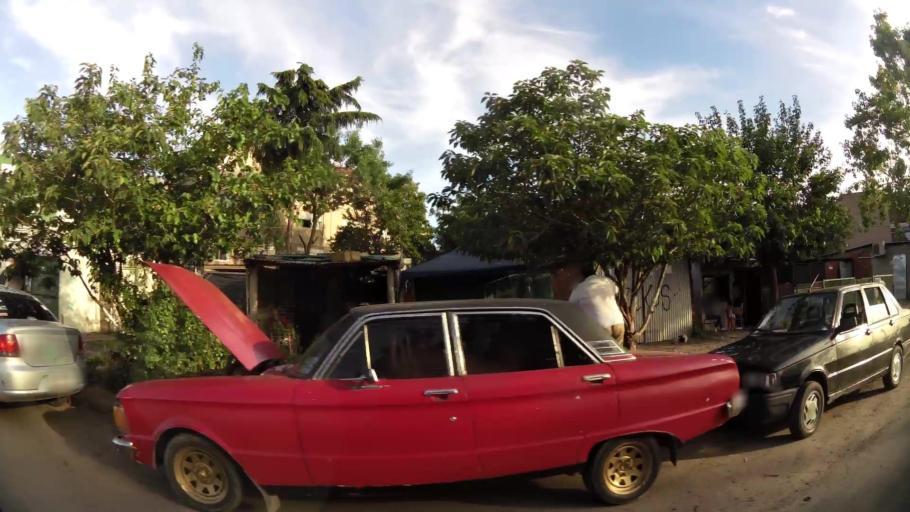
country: AR
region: Buenos Aires
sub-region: Partido de Almirante Brown
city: Adrogue
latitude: -34.8176
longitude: -58.3394
